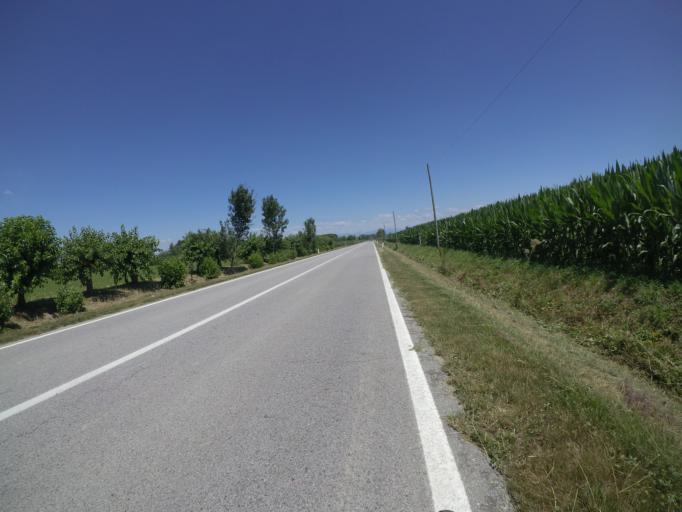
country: IT
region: Friuli Venezia Giulia
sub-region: Provincia di Udine
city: Rivignano
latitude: 45.8907
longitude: 13.0784
